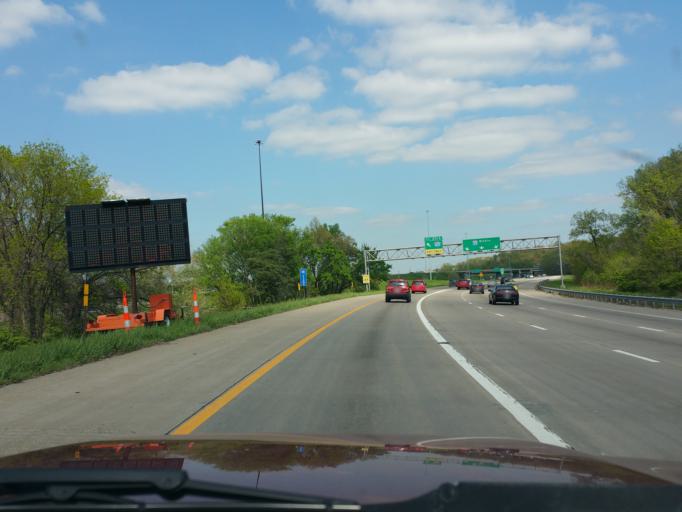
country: US
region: Kansas
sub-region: Johnson County
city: Merriam
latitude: 39.0384
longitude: -94.6800
